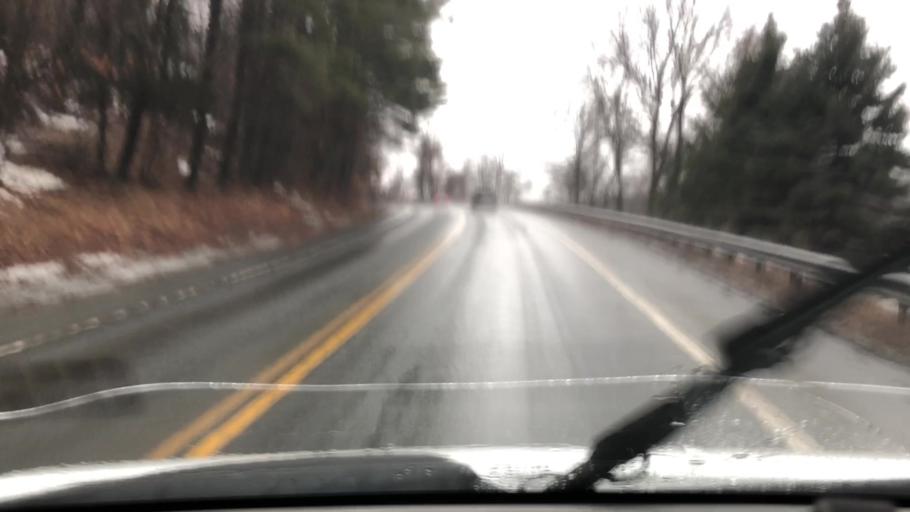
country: US
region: Massachusetts
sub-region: Franklin County
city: Shelburne Falls
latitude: 42.5885
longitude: -72.7180
